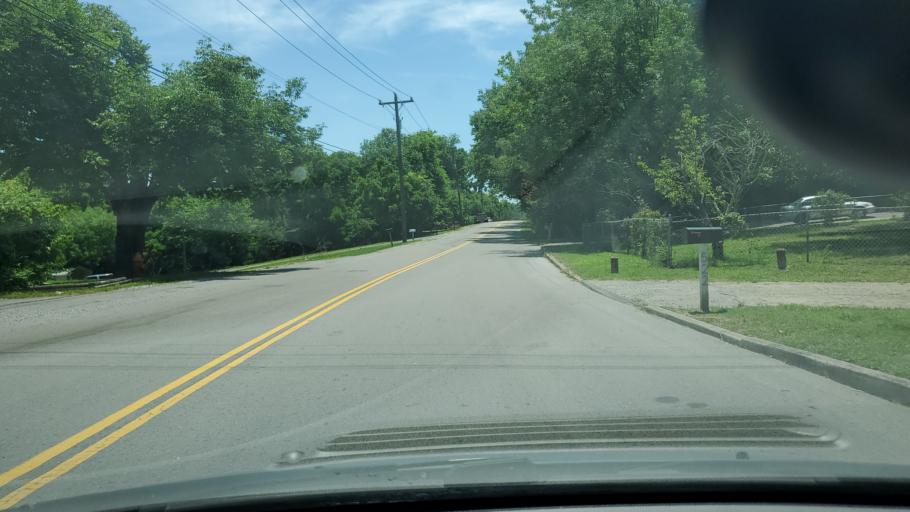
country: US
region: Tennessee
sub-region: Davidson County
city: Nashville
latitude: 36.2203
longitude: -86.7442
